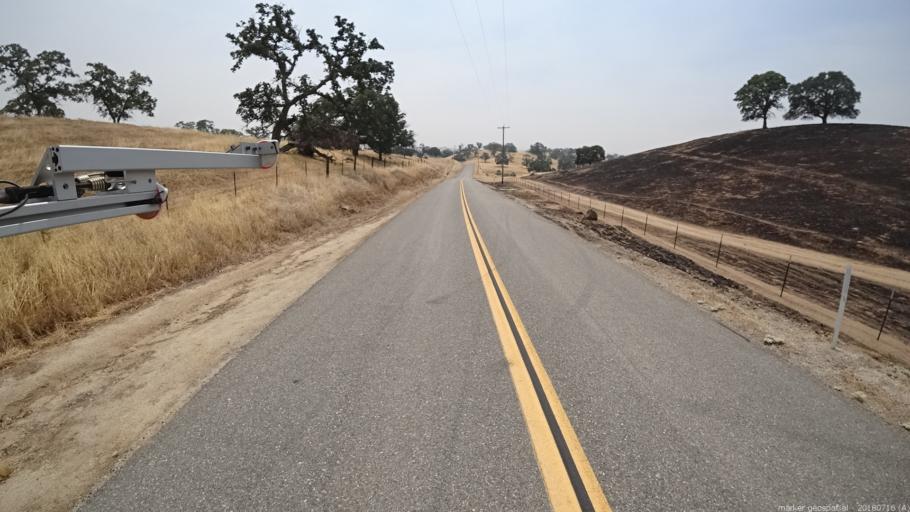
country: US
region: California
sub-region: Madera County
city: Yosemite Lakes
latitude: 37.1441
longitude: -119.9090
